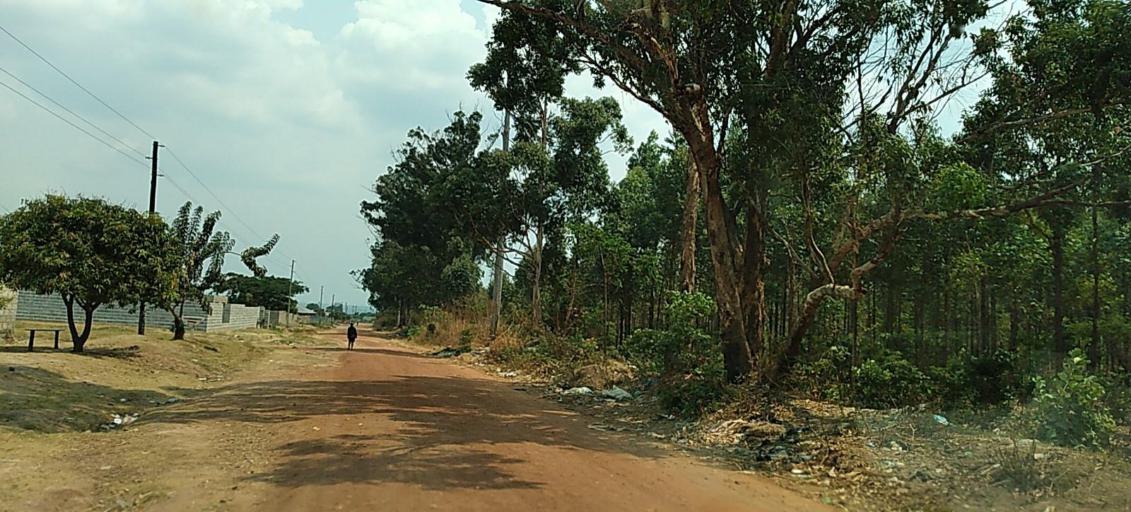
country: ZM
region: Copperbelt
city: Kalulushi
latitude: -12.8478
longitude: 28.0780
